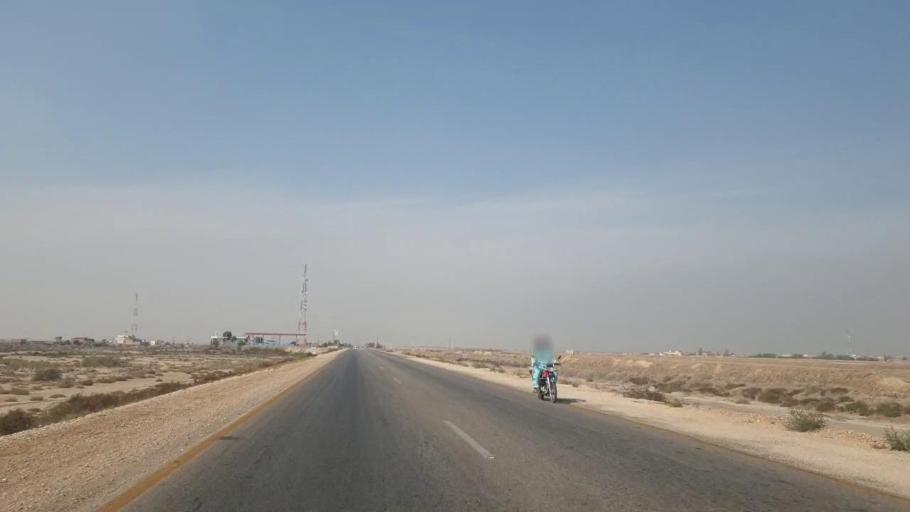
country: PK
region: Sindh
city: Sann
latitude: 25.8978
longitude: 68.2349
